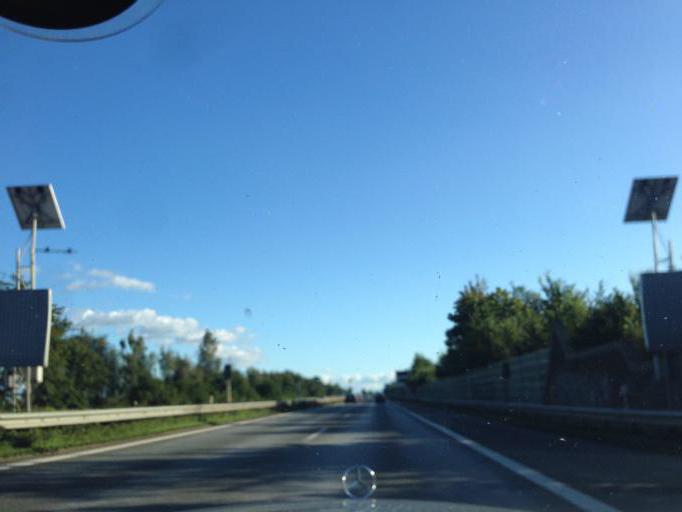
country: DE
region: Schleswig-Holstein
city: Padenstedt
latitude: 54.0523
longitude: 9.9257
